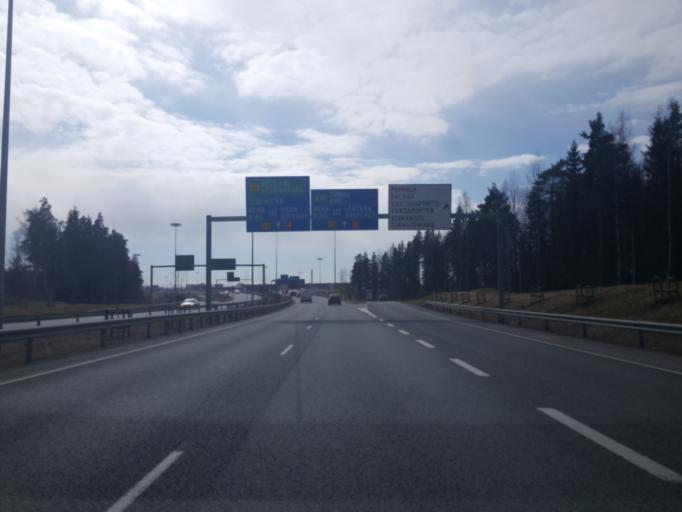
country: FI
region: Uusimaa
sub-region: Helsinki
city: Vantaa
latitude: 60.3006
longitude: 24.9599
